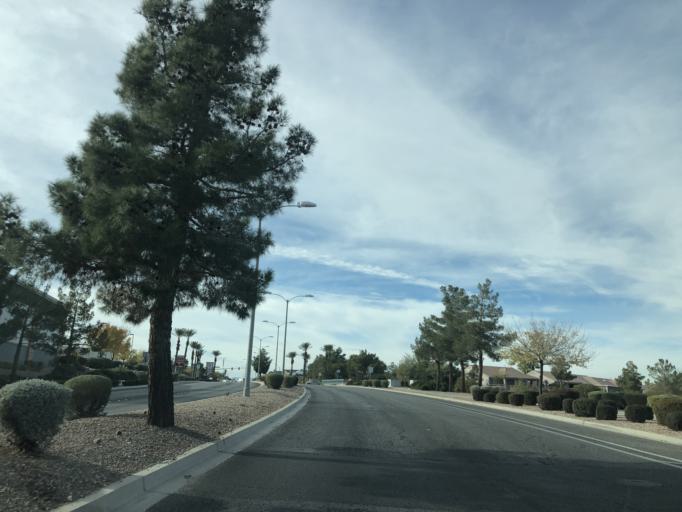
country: US
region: Nevada
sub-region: Clark County
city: Whitney
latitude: 36.0057
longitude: -115.0797
